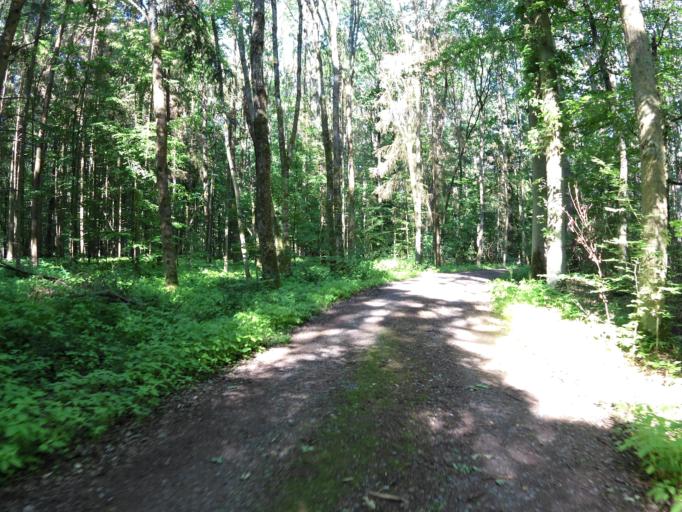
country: DE
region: Bavaria
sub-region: Regierungsbezirk Unterfranken
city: Reichenberg
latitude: 49.7300
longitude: 9.8954
